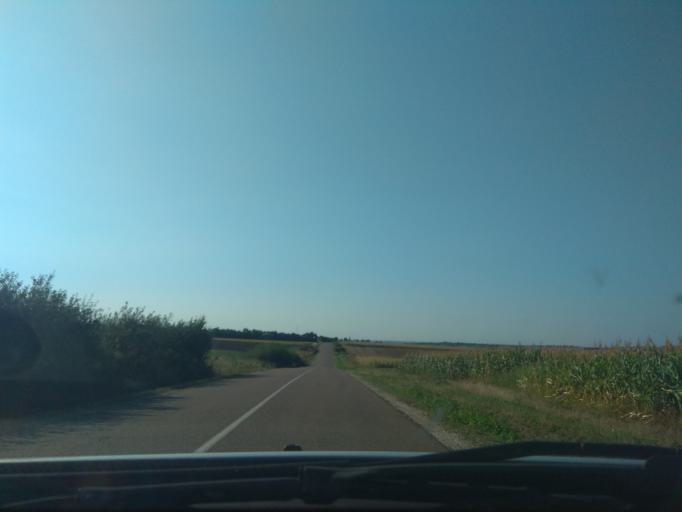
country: HU
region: Borsod-Abauj-Zemplen
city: Emod
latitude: 47.9663
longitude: 20.8003
